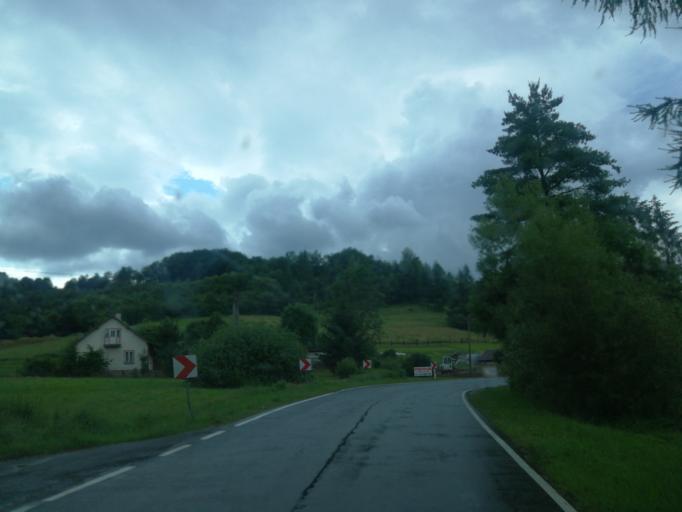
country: PL
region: Subcarpathian Voivodeship
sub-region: Powiat leski
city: Polanczyk
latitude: 49.4183
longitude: 22.4484
